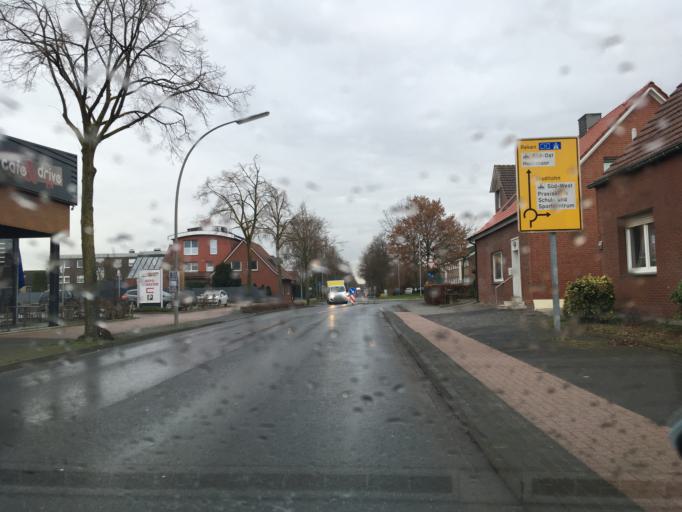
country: DE
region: North Rhine-Westphalia
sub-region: Regierungsbezirk Munster
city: Gescher
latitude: 51.9487
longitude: 7.0161
